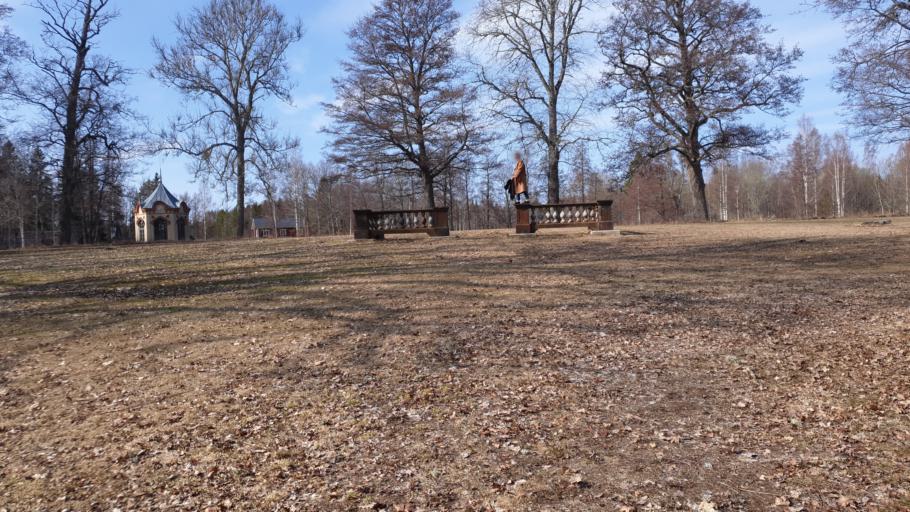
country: SE
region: Gaevleborg
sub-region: Gavle Kommun
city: Norrsundet
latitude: 61.0458
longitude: 17.1426
